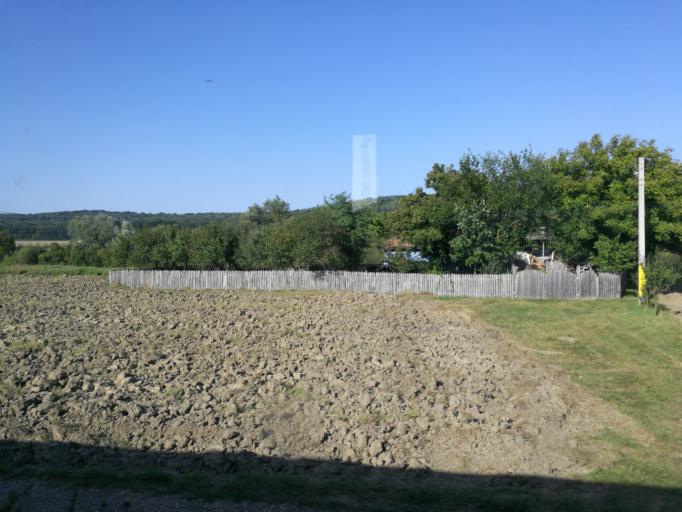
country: RO
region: Iasi
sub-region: Comuna Grajduri
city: Grajduri
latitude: 46.9580
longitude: 27.5577
